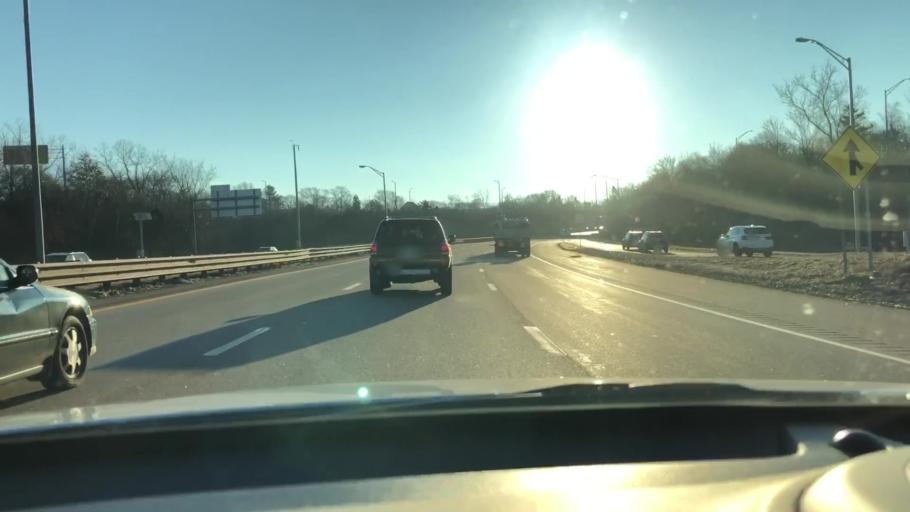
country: US
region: Massachusetts
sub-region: Norfolk County
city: Braintree
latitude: 42.2271
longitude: -71.0070
